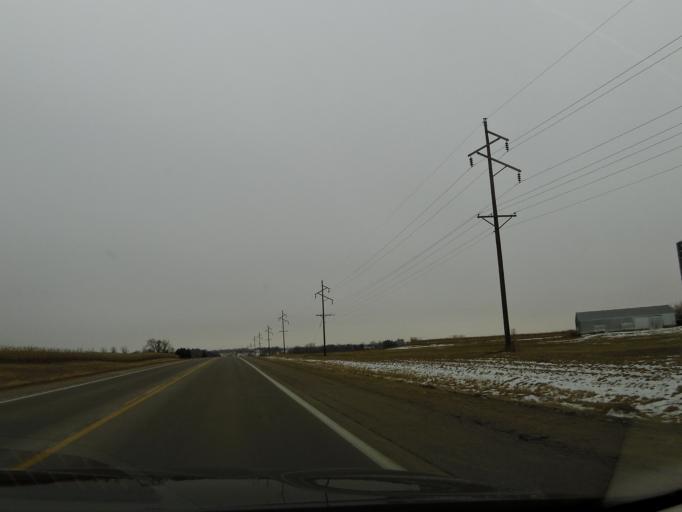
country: US
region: Minnesota
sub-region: Scott County
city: Jordan
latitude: 44.6365
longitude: -93.6168
